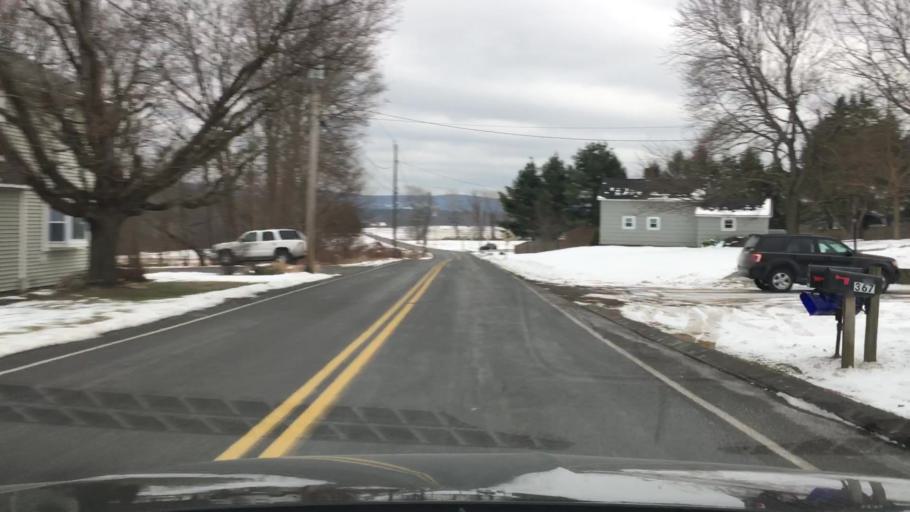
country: US
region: Connecticut
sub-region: Tolland County
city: Somers
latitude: 42.0047
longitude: -72.4789
